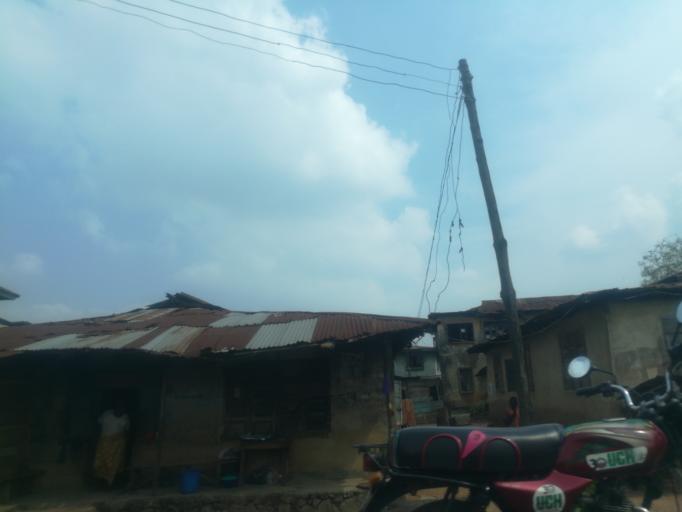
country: NG
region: Oyo
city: Ibadan
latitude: 7.3926
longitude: 3.9053
